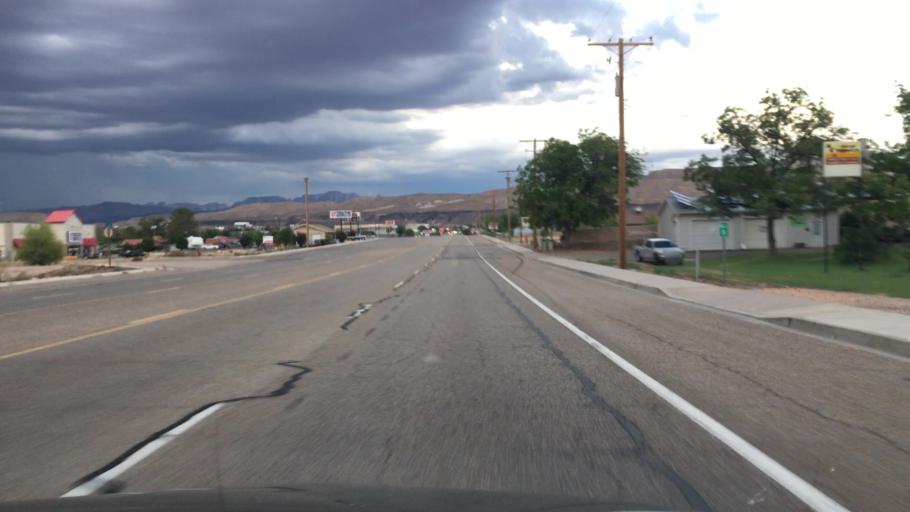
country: US
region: Utah
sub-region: Washington County
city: Hurricane
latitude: 37.1763
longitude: -113.3205
